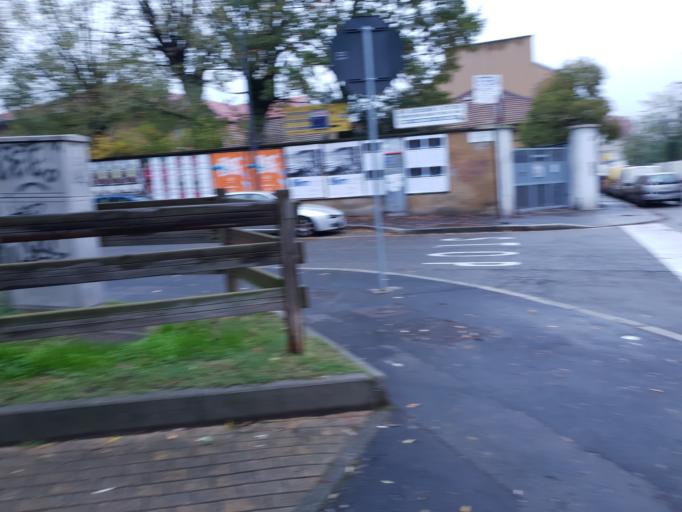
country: IT
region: Lombardy
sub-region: Citta metropolitana di Milano
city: Bresso
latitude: 45.5034
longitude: 9.1697
